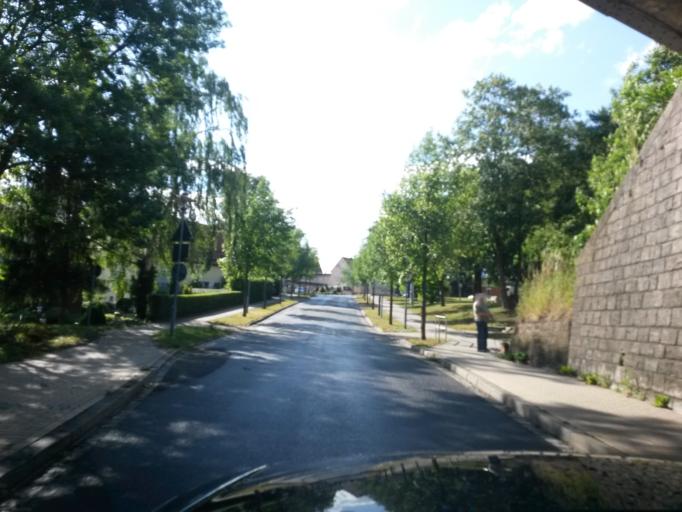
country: DE
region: Bavaria
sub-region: Regierungsbezirk Unterfranken
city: Rottendorf
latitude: 49.7899
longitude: 10.0291
